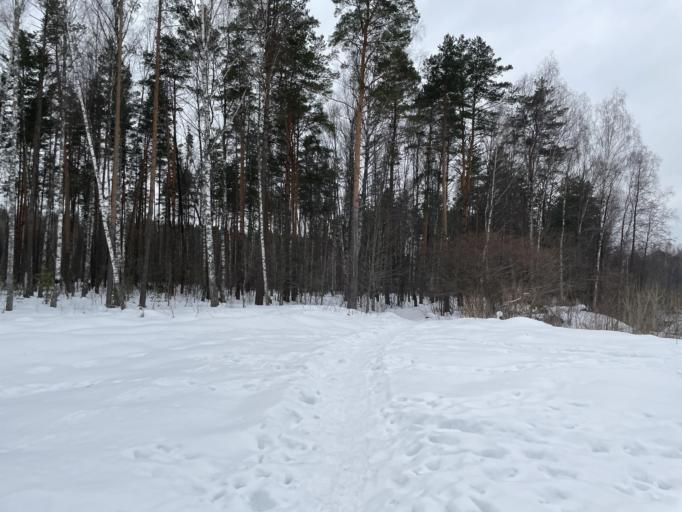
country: RU
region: Vladimir
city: Pokrov
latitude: 55.9427
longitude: 39.2395
